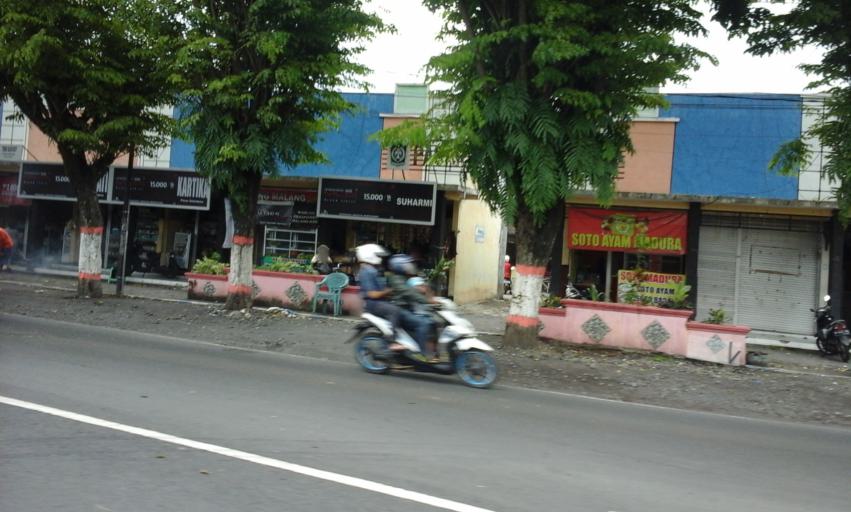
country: ID
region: East Java
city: Sukodono
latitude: -8.1040
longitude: 113.2324
